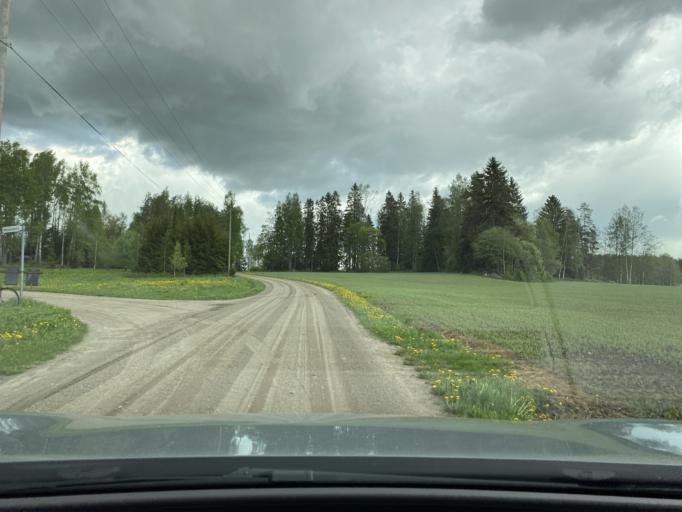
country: FI
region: Paijanne Tavastia
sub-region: Lahti
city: Jaervelae
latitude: 60.7700
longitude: 25.4314
